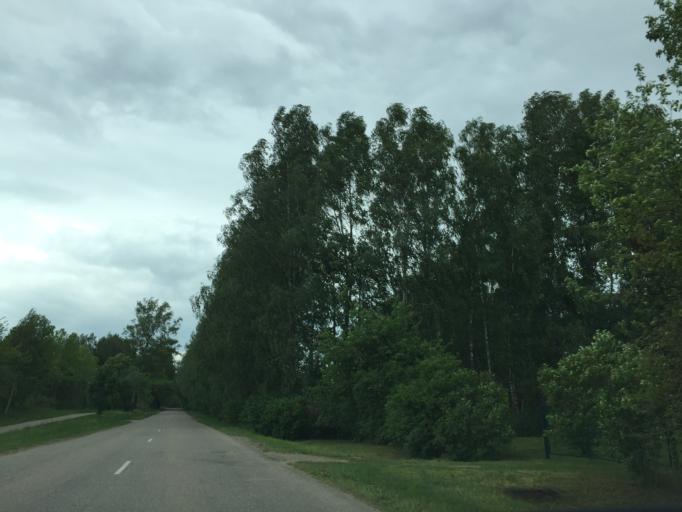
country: LV
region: Preilu Rajons
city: Preili
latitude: 56.0603
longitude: 26.7730
